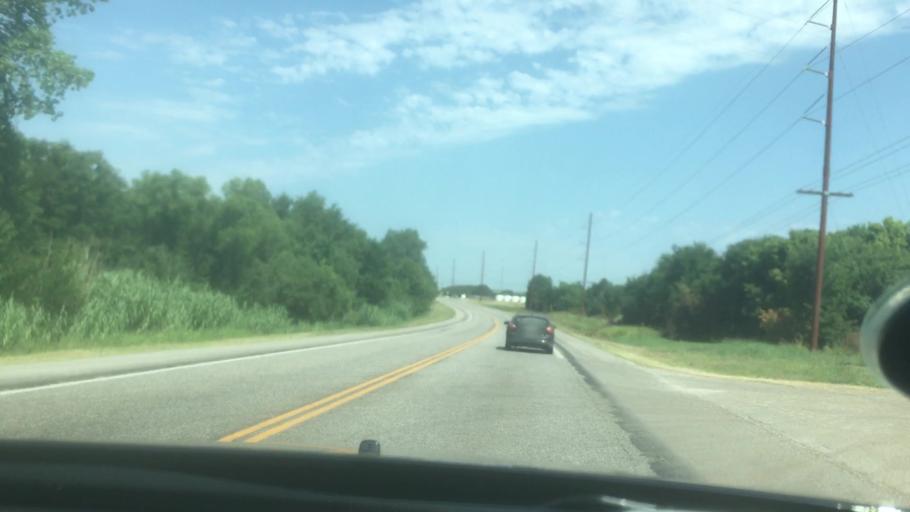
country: US
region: Oklahoma
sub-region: Seminole County
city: Konawa
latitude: 34.8616
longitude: -96.8250
